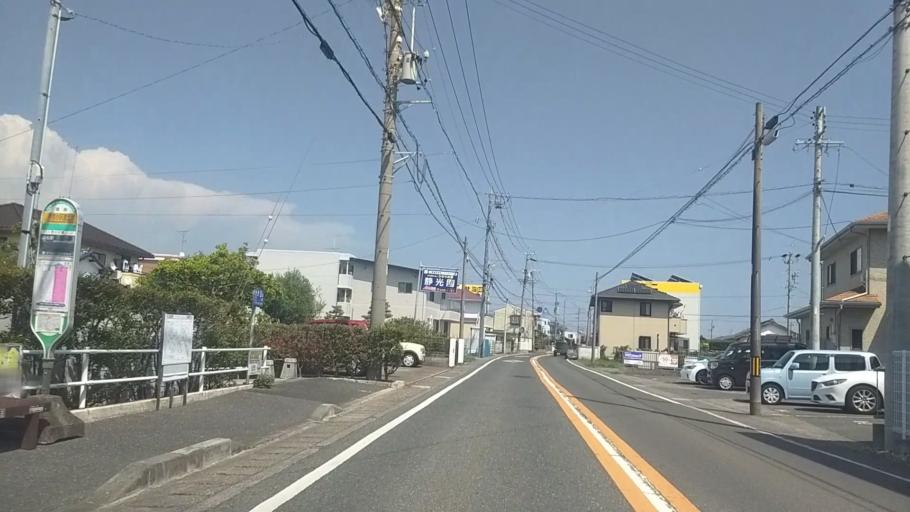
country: JP
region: Shizuoka
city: Hamamatsu
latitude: 34.6835
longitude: 137.6774
